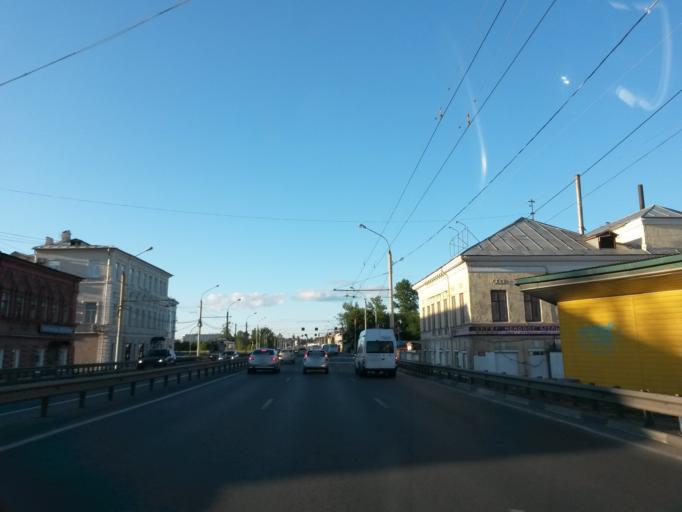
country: RU
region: Jaroslavl
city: Yaroslavl
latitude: 57.6105
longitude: 39.8819
